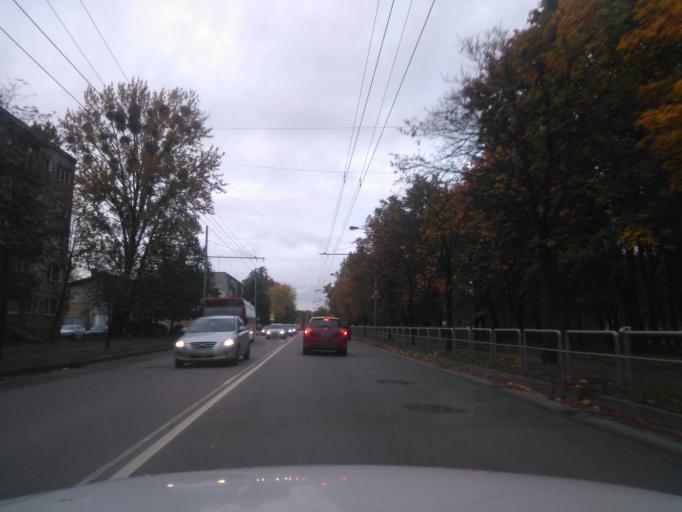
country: LT
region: Kauno apskritis
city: Dainava (Kaunas)
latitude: 54.9088
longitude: 23.9738
